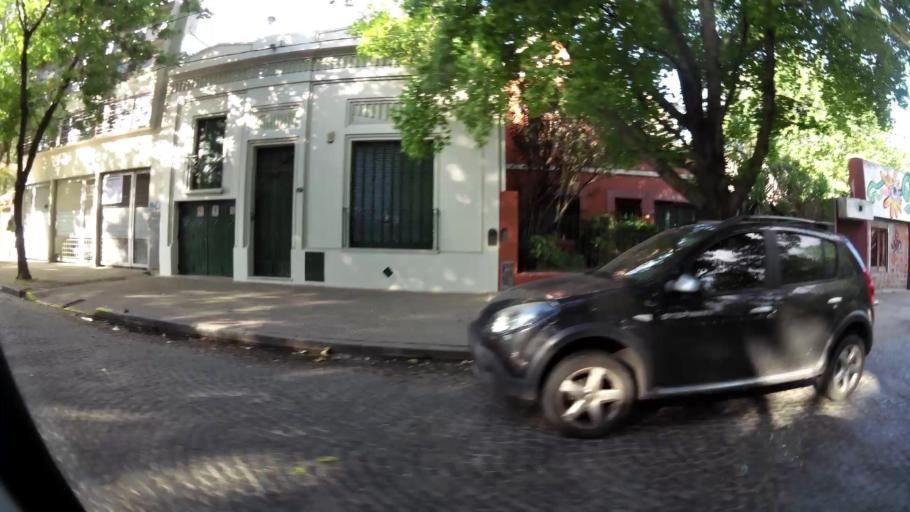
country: AR
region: Buenos Aires
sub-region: Partido de La Plata
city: La Plata
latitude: -34.8993
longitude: -57.9557
